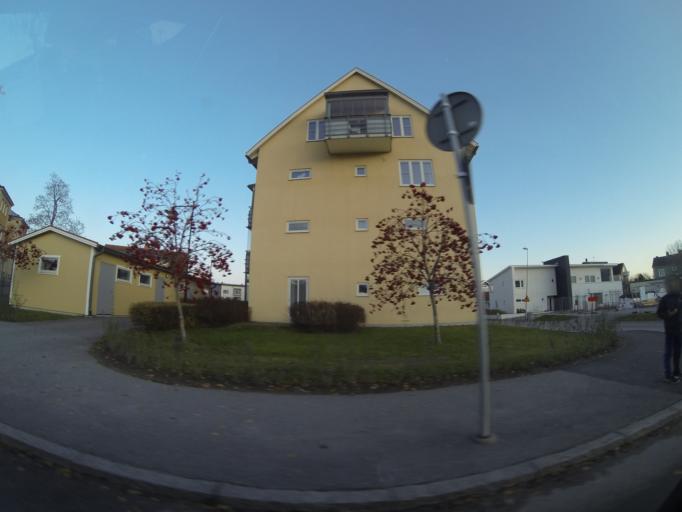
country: SE
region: OErebro
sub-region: Orebro Kommun
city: Orebro
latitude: 59.2823
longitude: 15.2366
